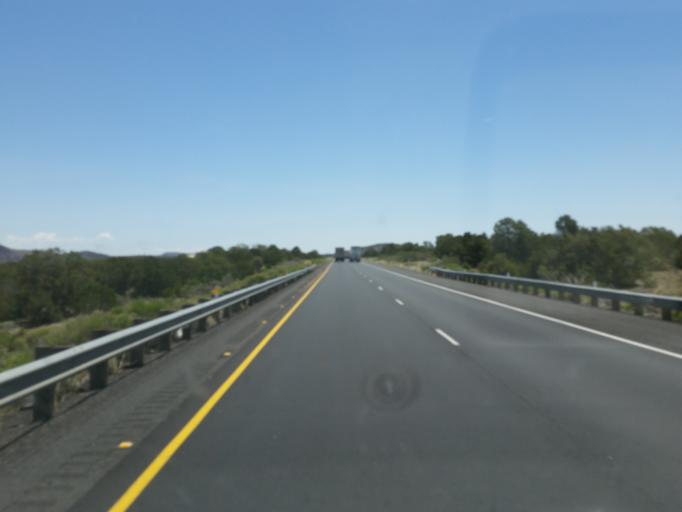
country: US
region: Arizona
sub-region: Coconino County
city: Flagstaff
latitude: 35.2019
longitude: -111.4534
